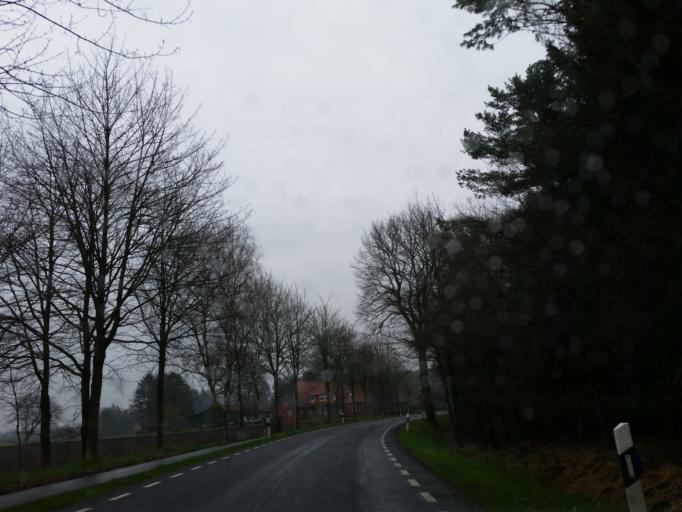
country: DE
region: Lower Saxony
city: Hipstedt
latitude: 53.5219
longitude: 8.9582
